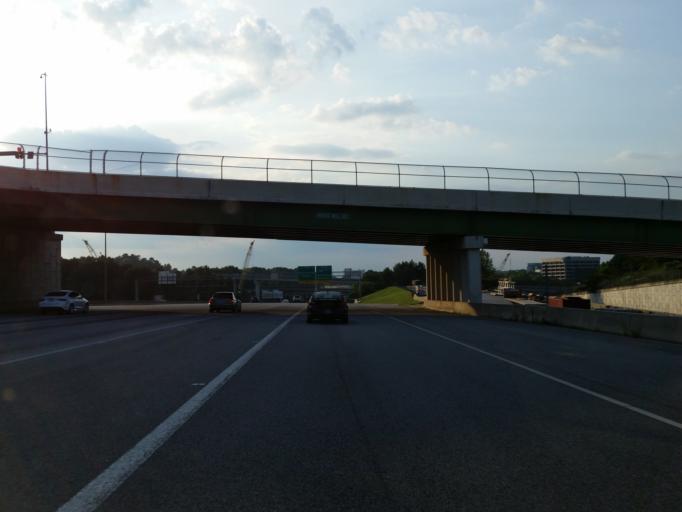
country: US
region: Georgia
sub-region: Cobb County
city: Vinings
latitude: 33.8862
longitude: -84.4571
